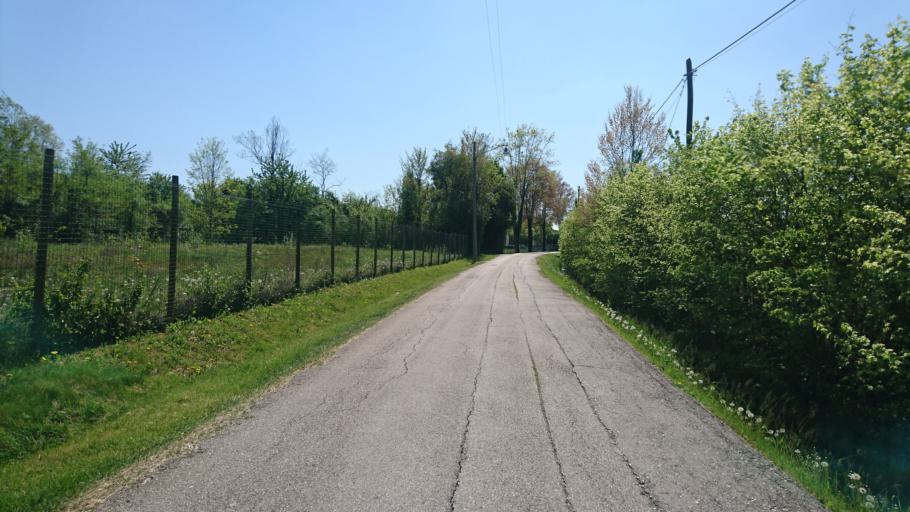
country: IT
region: Veneto
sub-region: Provincia di Treviso
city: Casier
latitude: 45.6397
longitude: 12.2744
